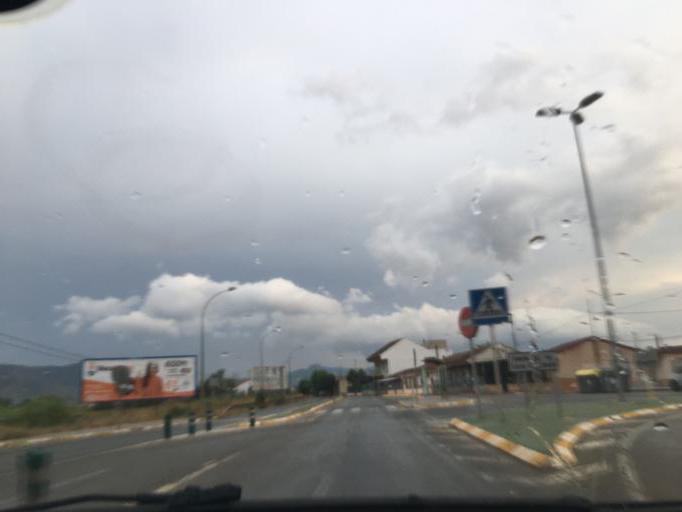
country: ES
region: Murcia
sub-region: Murcia
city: Santomera
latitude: 38.0230
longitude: -1.0454
